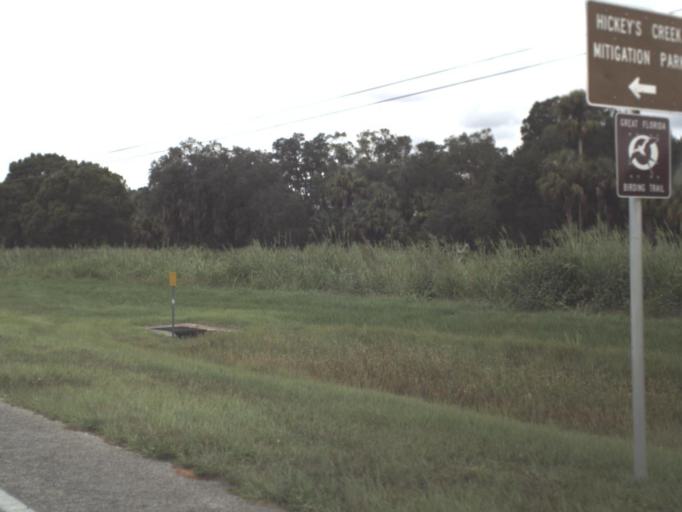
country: US
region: Florida
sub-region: Lee County
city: Olga
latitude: 26.7139
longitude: -81.6630
